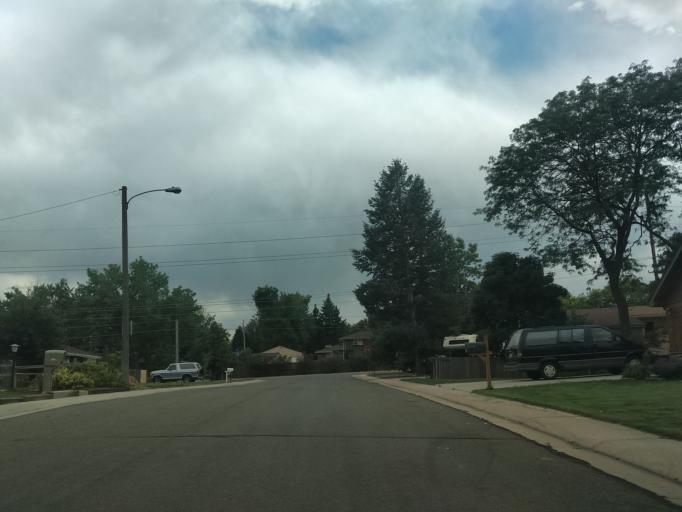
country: US
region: Colorado
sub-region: Jefferson County
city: Lakewood
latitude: 39.6975
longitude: -105.0963
